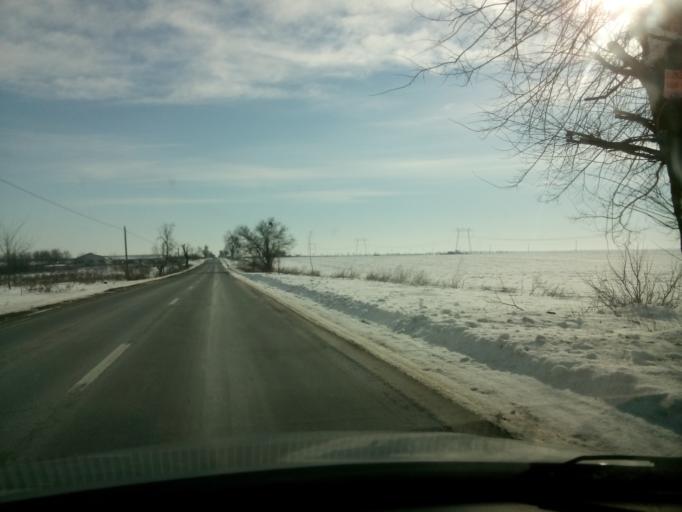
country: RO
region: Calarasi
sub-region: Comuna Frumusani
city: Frumusani
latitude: 44.2681
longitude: 26.3477
